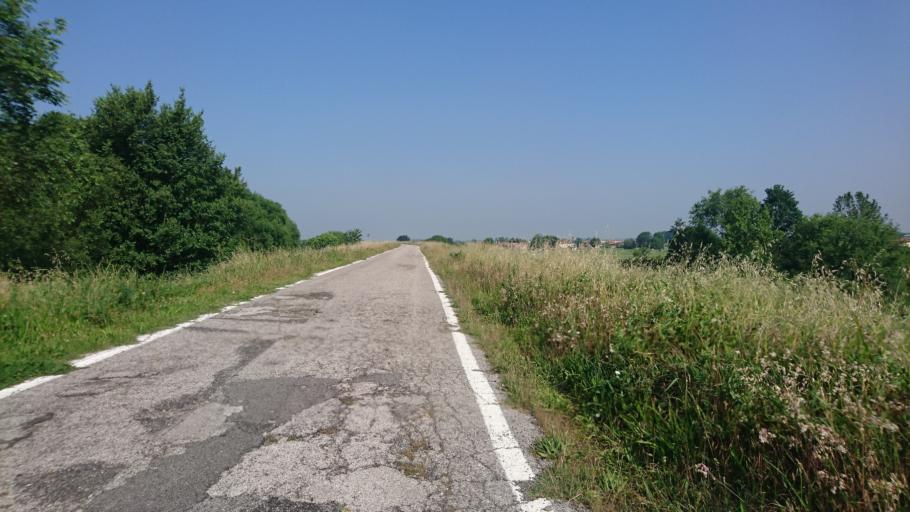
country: IT
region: Lombardy
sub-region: Provincia di Mantova
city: Borgofranco sul Po
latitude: 45.0557
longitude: 11.2234
